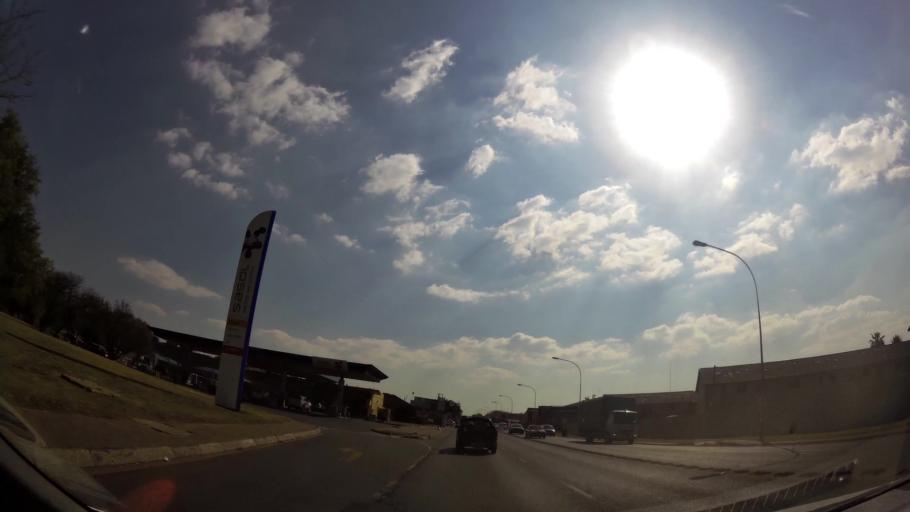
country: ZA
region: Gauteng
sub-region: Ekurhuleni Metropolitan Municipality
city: Boksburg
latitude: -26.1961
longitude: 28.2431
